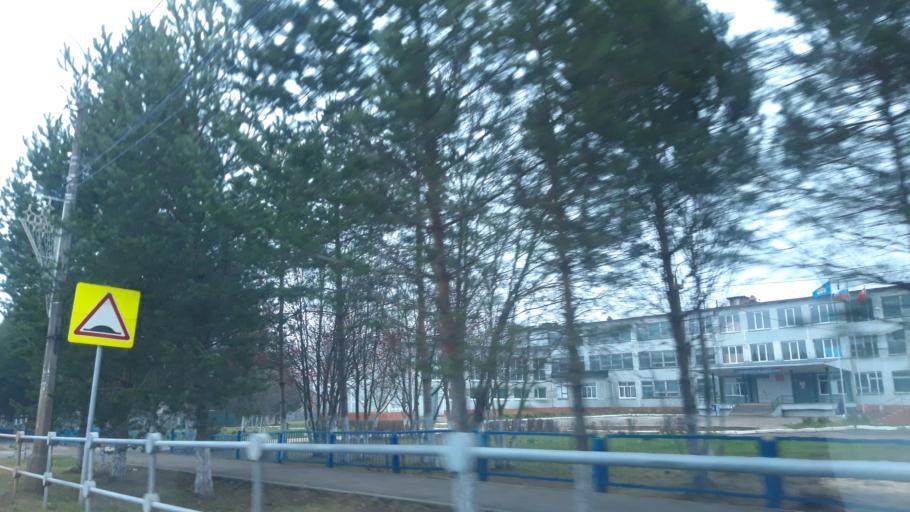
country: RU
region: Moskovskaya
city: Solnechnogorsk
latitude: 56.0797
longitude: 36.9125
